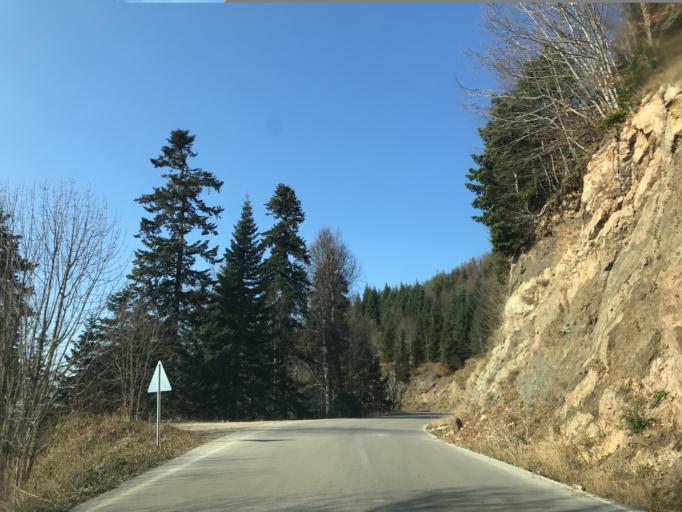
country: TR
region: Bolu
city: Bolu
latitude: 40.8858
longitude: 31.6823
